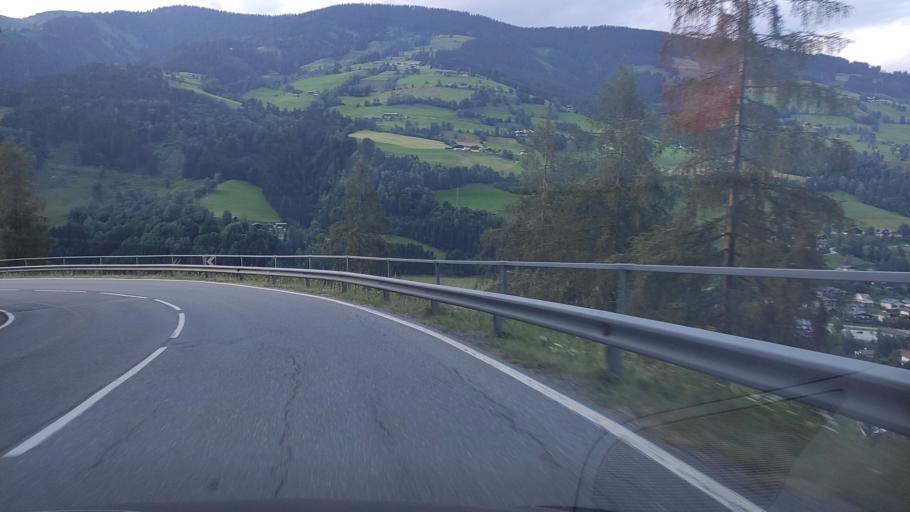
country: AT
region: Salzburg
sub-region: Politischer Bezirk Zell am See
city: Taxenbach
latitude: 47.2863
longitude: 12.9544
